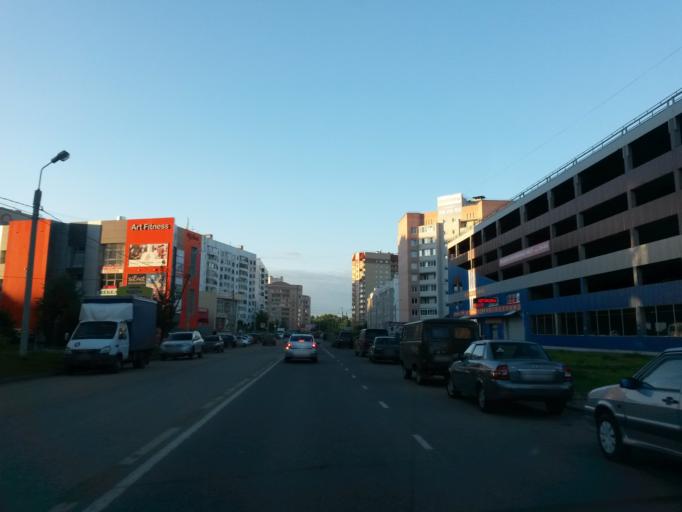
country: RU
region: Jaroslavl
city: Yaroslavl
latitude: 57.6936
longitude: 39.7797
